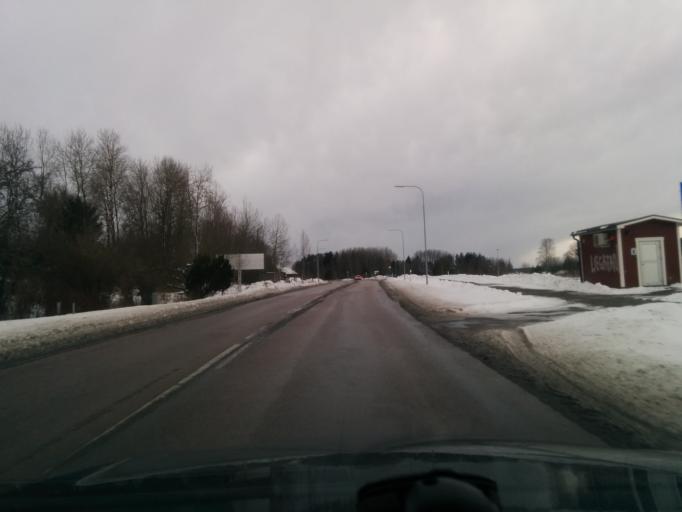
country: SE
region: Vaestmanland
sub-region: Vasteras
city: Vasteras
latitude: 59.5882
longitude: 16.4413
